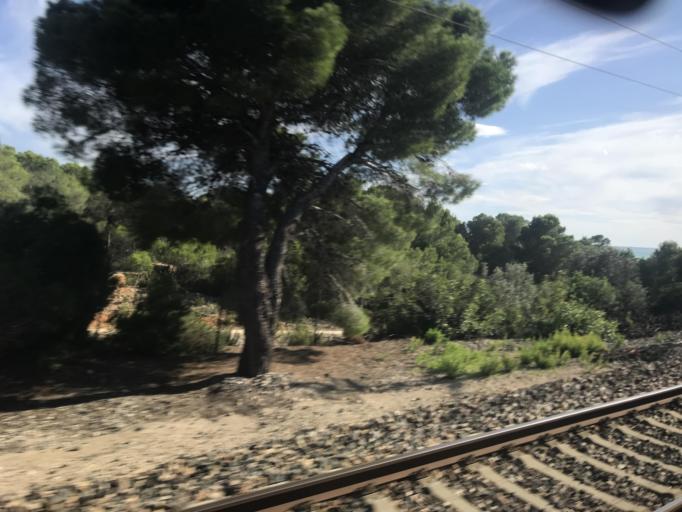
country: ES
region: Catalonia
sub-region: Provincia de Tarragona
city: l'Ametlla de Mar
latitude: 40.8574
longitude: 0.7677
